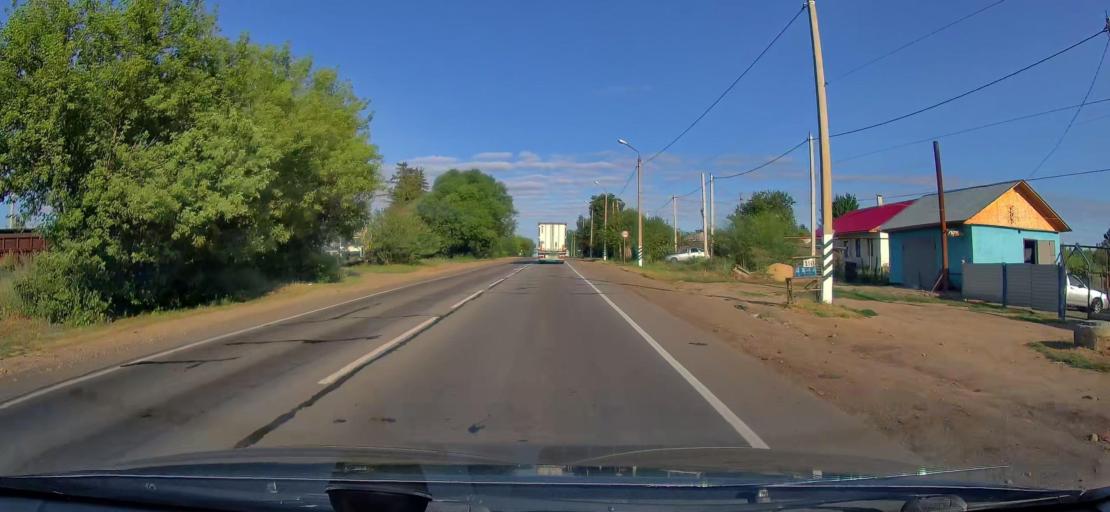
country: RU
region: Tula
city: Chern'
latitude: 53.4526
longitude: 36.8797
